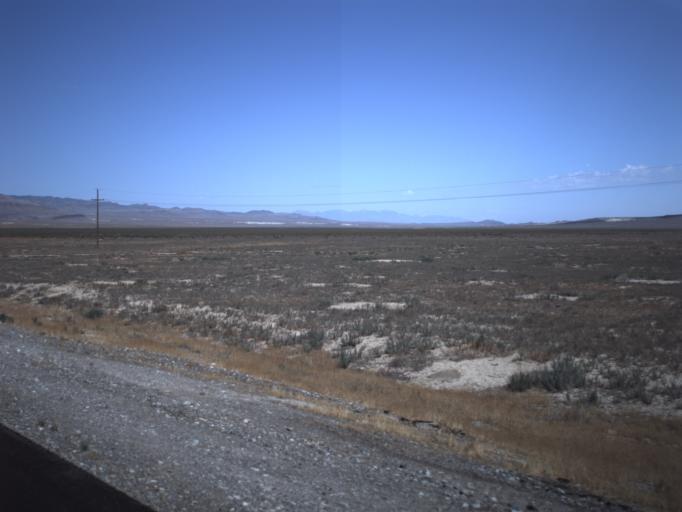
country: US
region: Utah
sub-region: Beaver County
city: Milford
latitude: 39.0698
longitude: -113.4600
